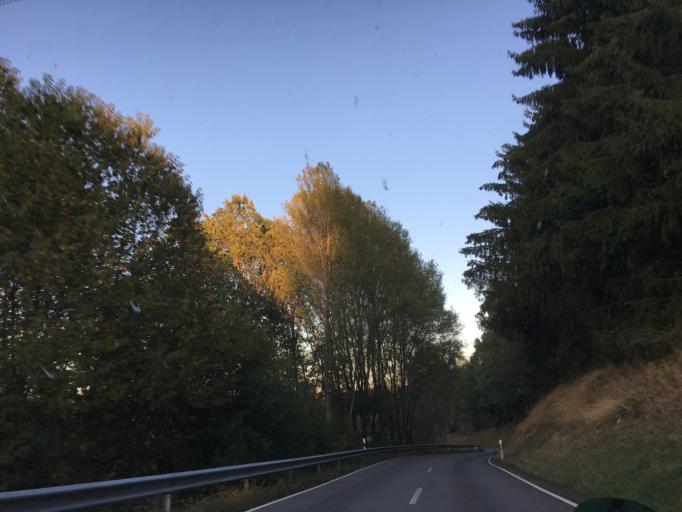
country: DE
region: Rheinland-Pfalz
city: Hermersberg
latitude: 49.3227
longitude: 7.6409
